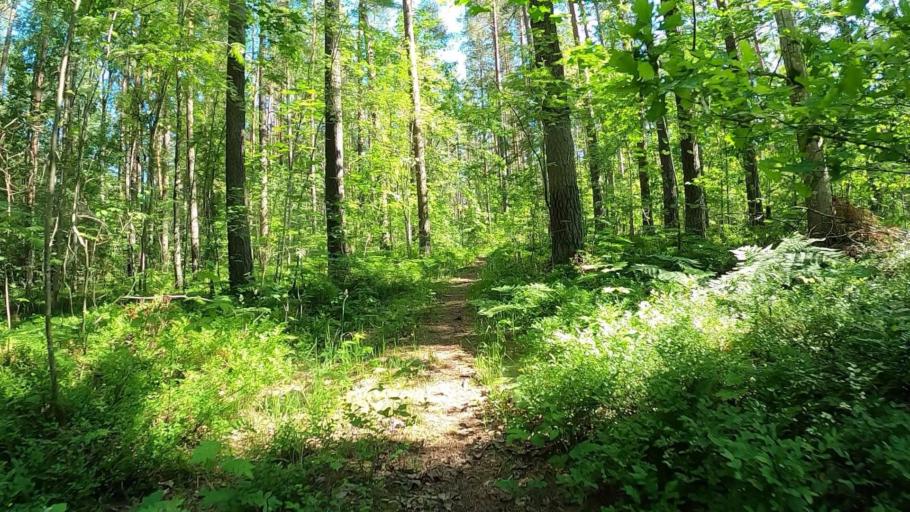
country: LV
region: Stopini
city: Ulbroka
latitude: 56.9194
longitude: 24.3062
